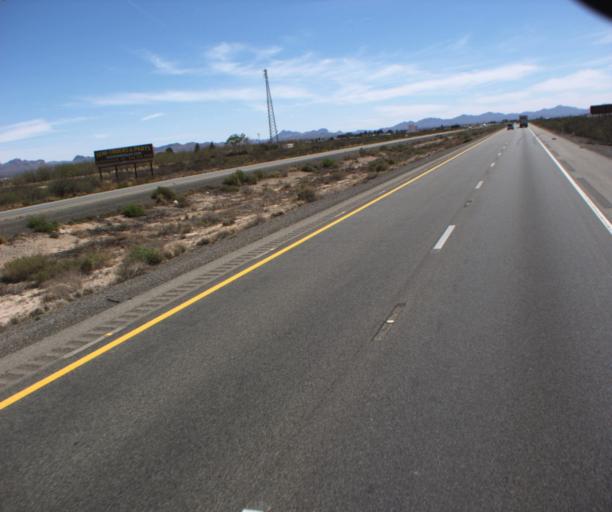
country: US
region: New Mexico
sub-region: Hidalgo County
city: Lordsburg
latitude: 32.2682
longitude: -109.2422
